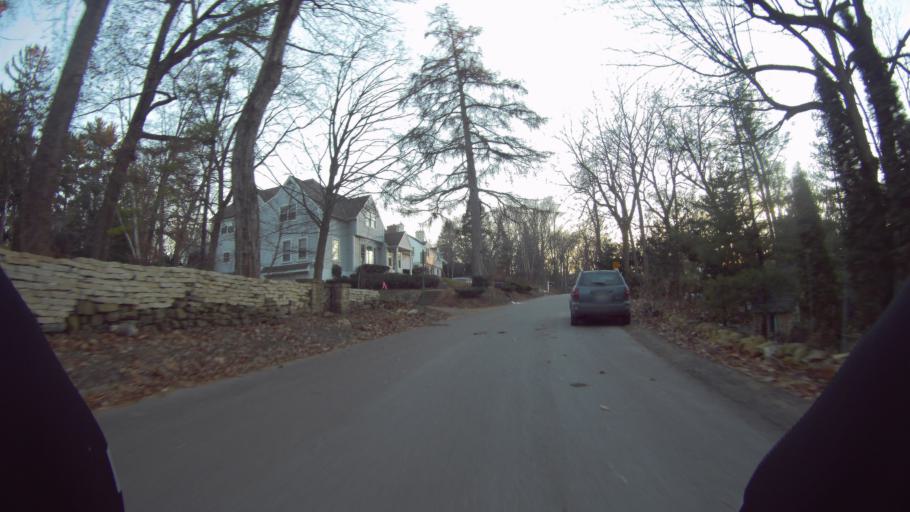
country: US
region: Wisconsin
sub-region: Dane County
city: Shorewood Hills
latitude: 43.0821
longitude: -89.4520
